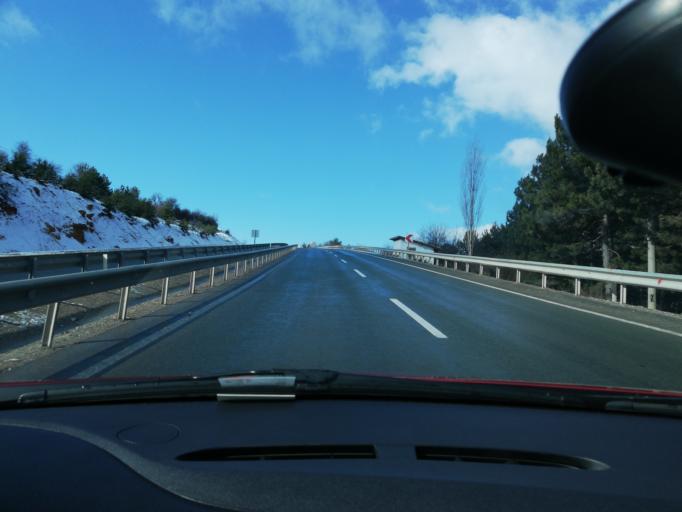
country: TR
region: Kastamonu
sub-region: Cide
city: Kastamonu
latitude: 41.3682
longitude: 33.7493
